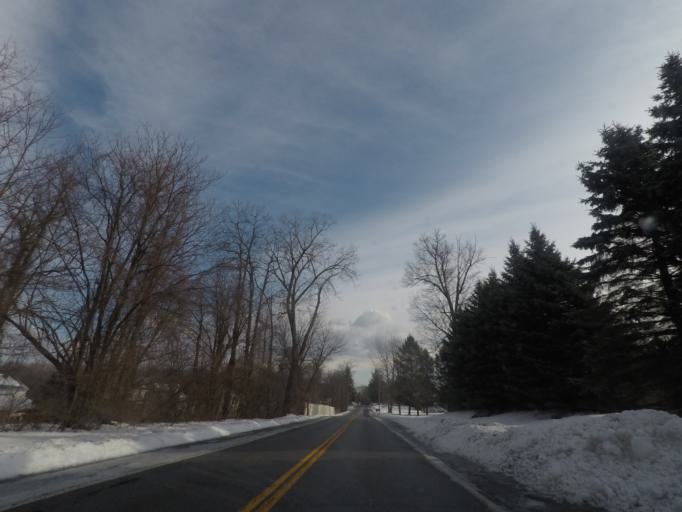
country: US
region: New York
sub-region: Saratoga County
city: Country Knolls
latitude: 42.8745
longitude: -73.7562
